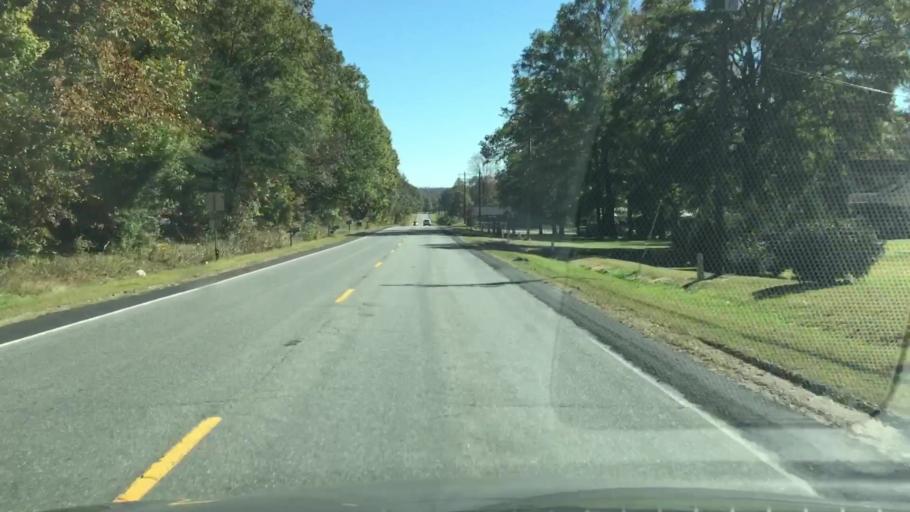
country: US
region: North Carolina
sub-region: Rockingham County
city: Reidsville
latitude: 36.2883
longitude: -79.6565
